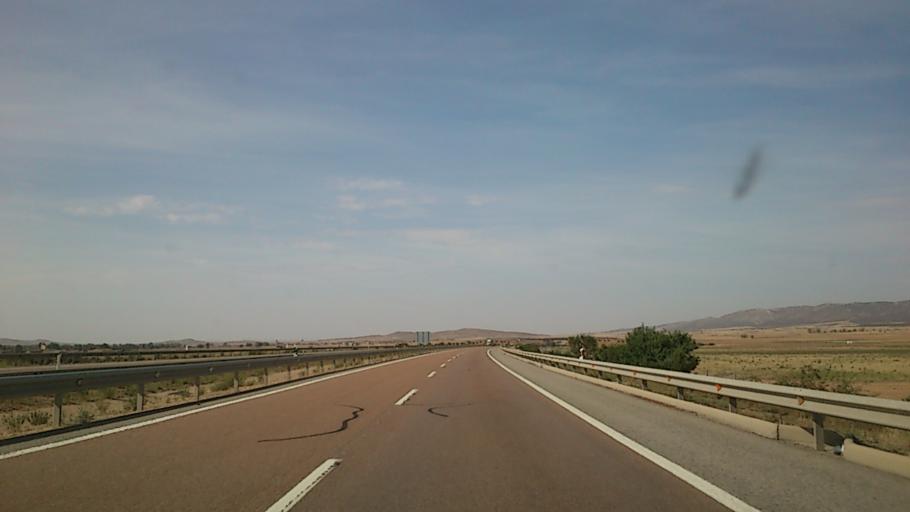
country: ES
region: Aragon
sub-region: Provincia de Teruel
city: Santa Eulalia
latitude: 40.5796
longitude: -1.2838
